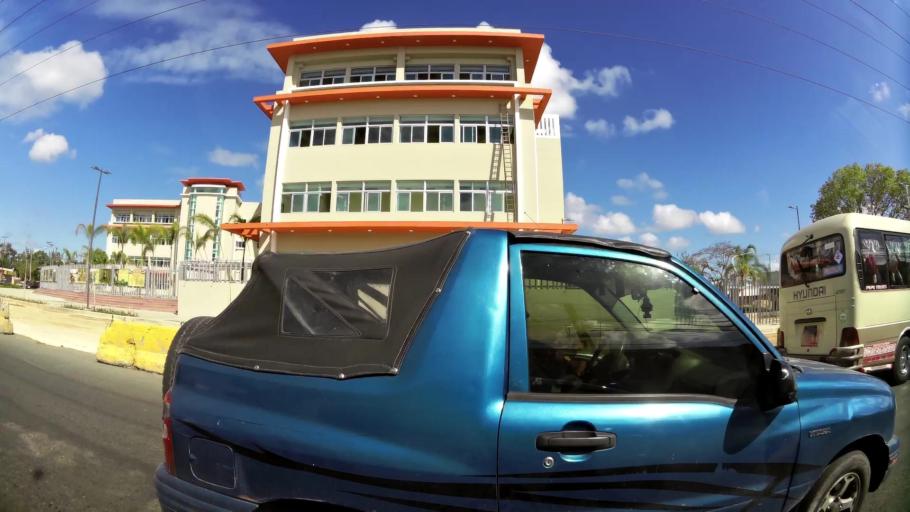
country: DO
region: Santo Domingo
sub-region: Santo Domingo
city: Santo Domingo Este
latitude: 18.5044
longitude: -69.8582
